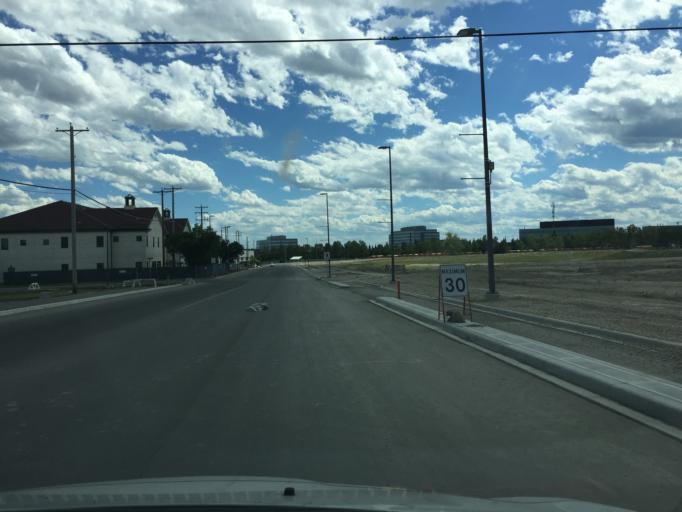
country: CA
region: Alberta
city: Calgary
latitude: 51.0174
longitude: -114.1238
